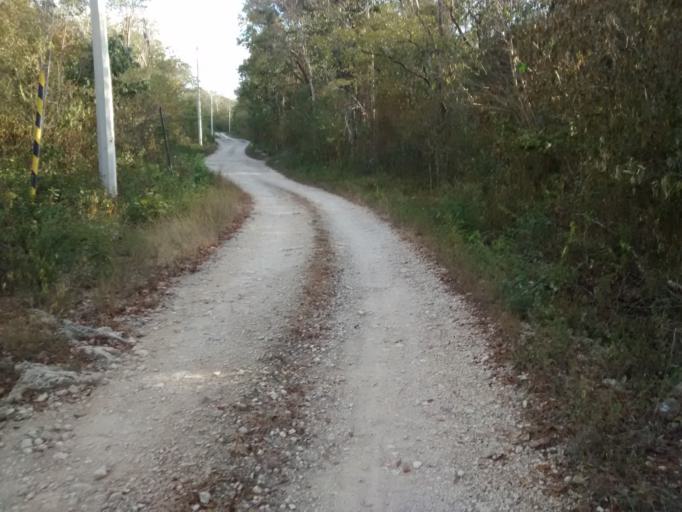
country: MX
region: Yucatan
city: Chichimila
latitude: 20.4519
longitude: -88.2034
